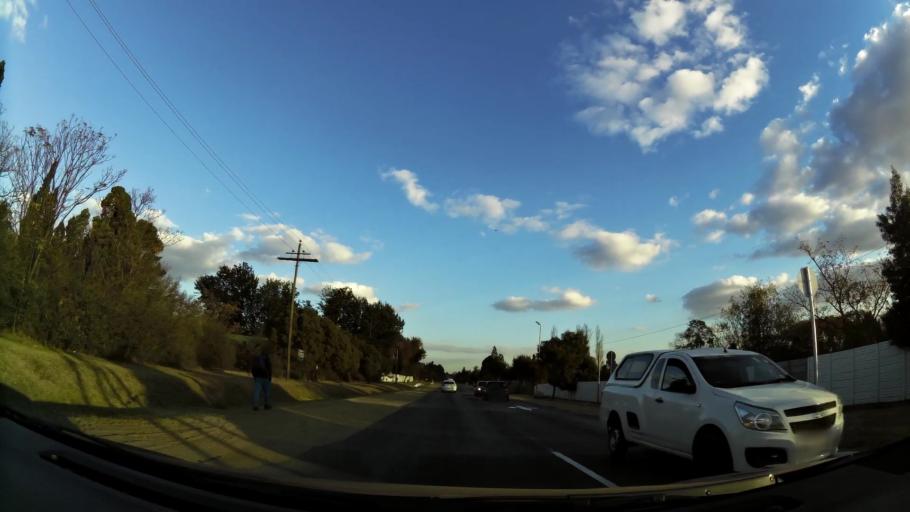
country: ZA
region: Gauteng
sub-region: City of Johannesburg Metropolitan Municipality
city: Midrand
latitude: -25.9748
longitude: 28.1532
